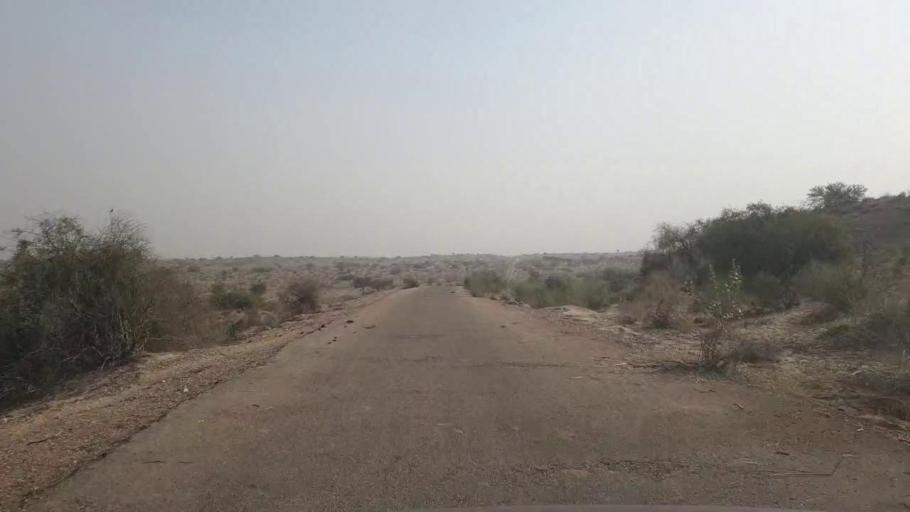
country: PK
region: Sindh
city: Chor
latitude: 25.5060
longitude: 69.9693
